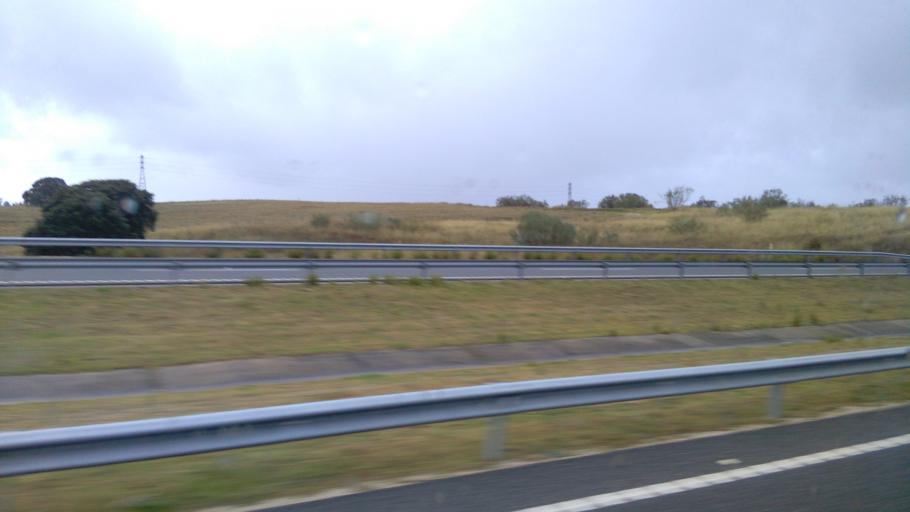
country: ES
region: Madrid
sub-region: Provincia de Madrid
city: Arroyomolinos
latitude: 40.2563
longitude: -3.9277
